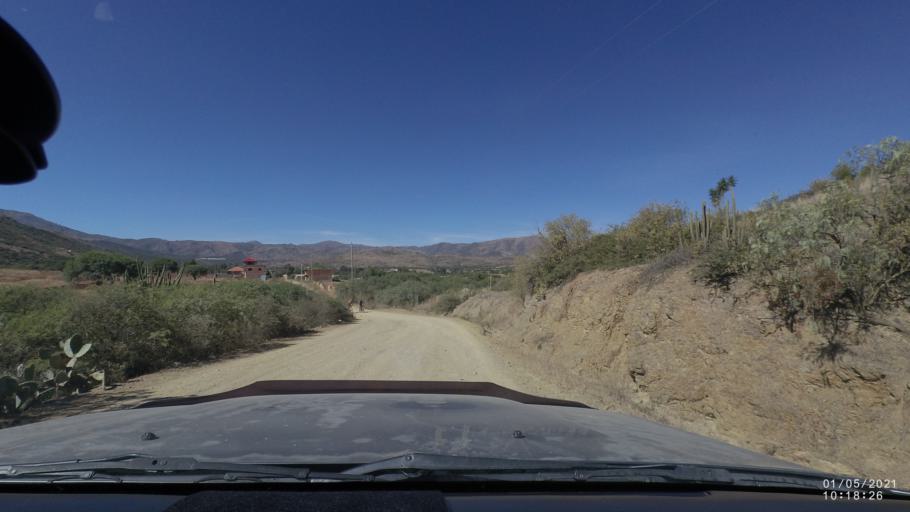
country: BO
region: Cochabamba
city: Capinota
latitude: -17.5547
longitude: -66.2086
